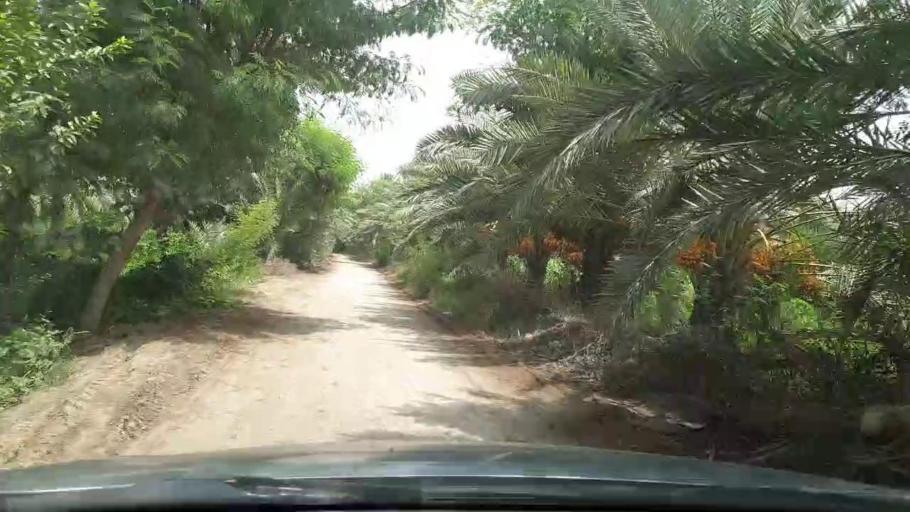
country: PK
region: Sindh
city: Kot Diji
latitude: 27.4294
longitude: 68.7501
